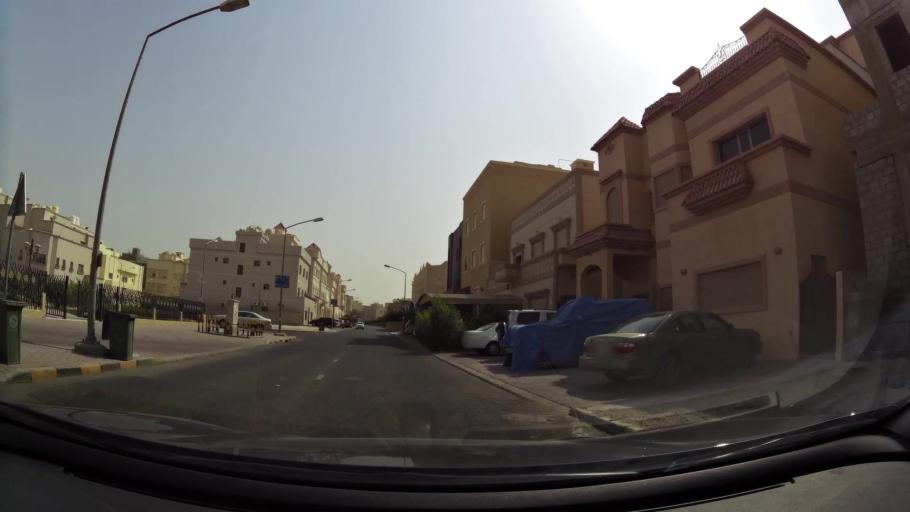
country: KW
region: Muhafazat al Jahra'
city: Al Jahra'
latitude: 29.3224
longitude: 47.7366
